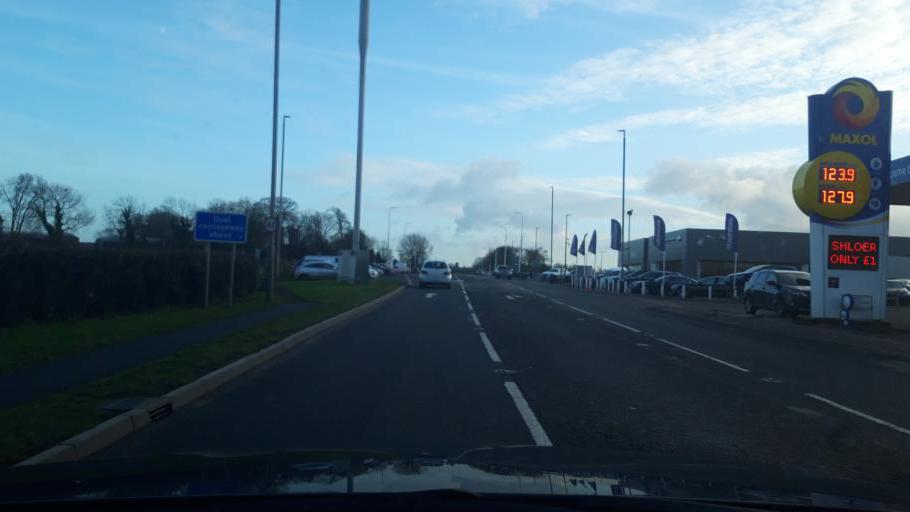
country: GB
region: Northern Ireland
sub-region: Dungannon District
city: Dungannon
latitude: 54.4871
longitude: -6.7448
